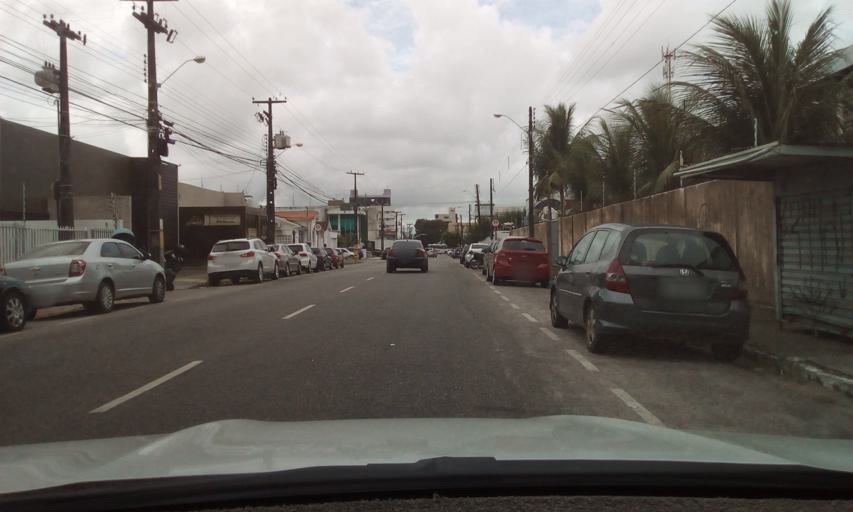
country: BR
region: Paraiba
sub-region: Joao Pessoa
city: Joao Pessoa
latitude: -7.1225
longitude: -34.8695
